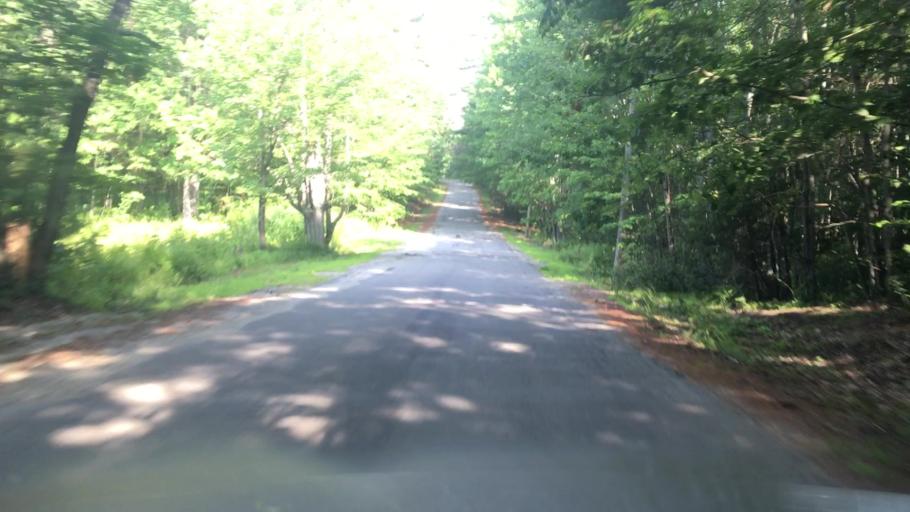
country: US
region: Maine
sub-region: Kennebec County
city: Monmouth
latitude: 44.2385
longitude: -70.0759
